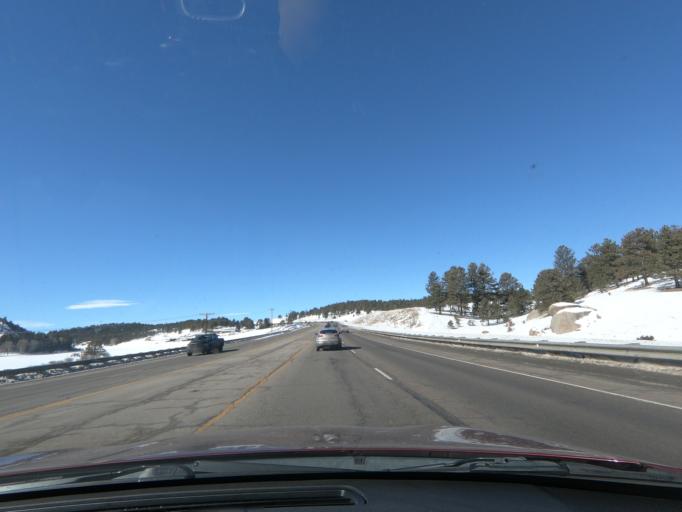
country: US
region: Colorado
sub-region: Teller County
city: Woodland Park
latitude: 38.9576
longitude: -105.1051
